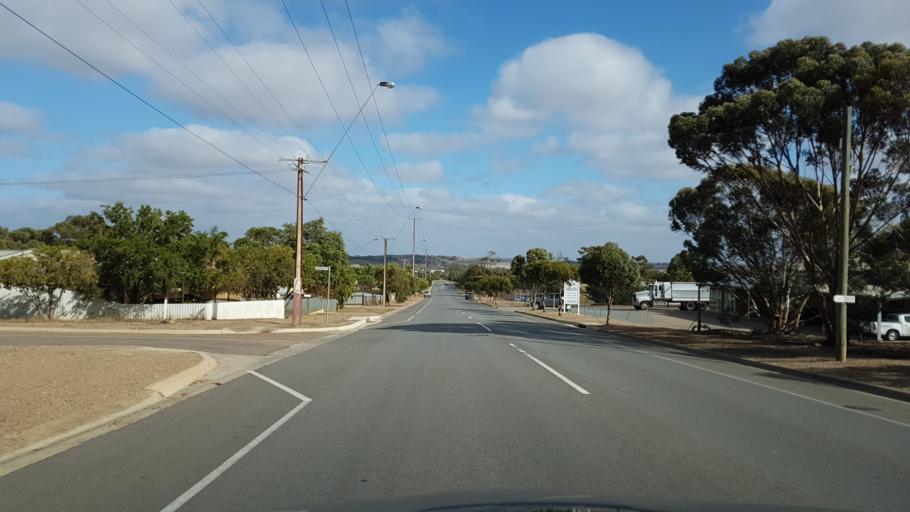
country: AU
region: South Australia
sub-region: Murray Bridge
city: Murray Bridge
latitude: -35.1201
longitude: 139.2509
